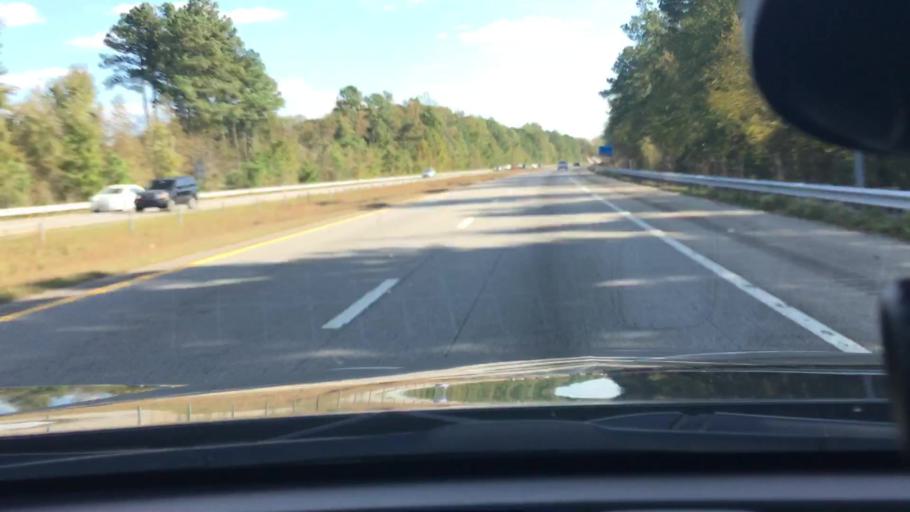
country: US
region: North Carolina
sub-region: Wilson County
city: Lucama
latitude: 35.7010
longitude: -77.9815
